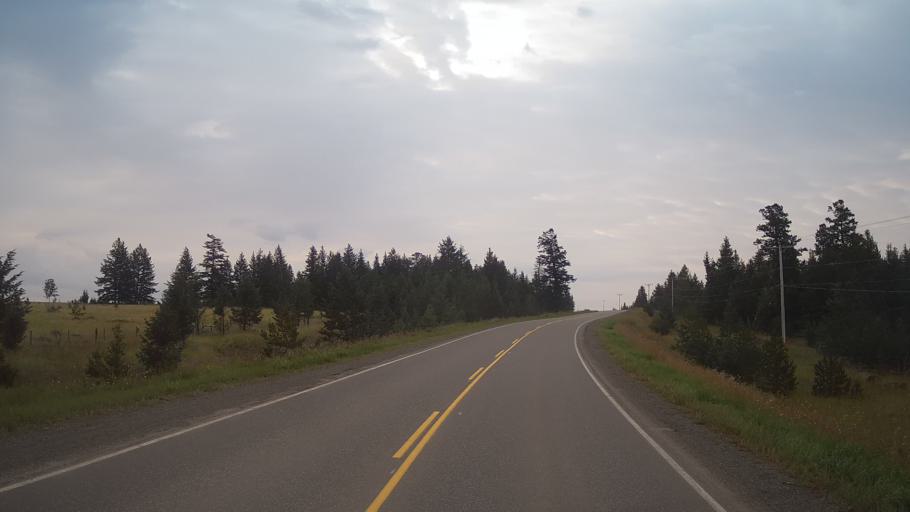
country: CA
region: British Columbia
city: Williams Lake
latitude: 51.9615
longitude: -122.3823
